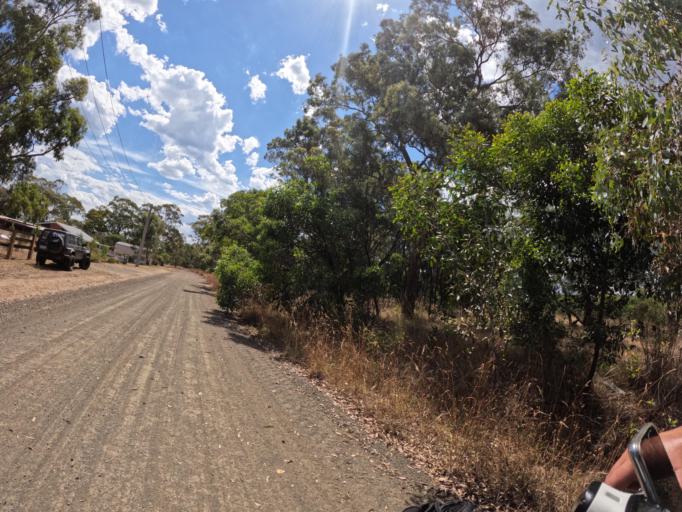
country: AU
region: Victoria
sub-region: Wellington
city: Heyfield
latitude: -37.9781
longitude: 146.7722
